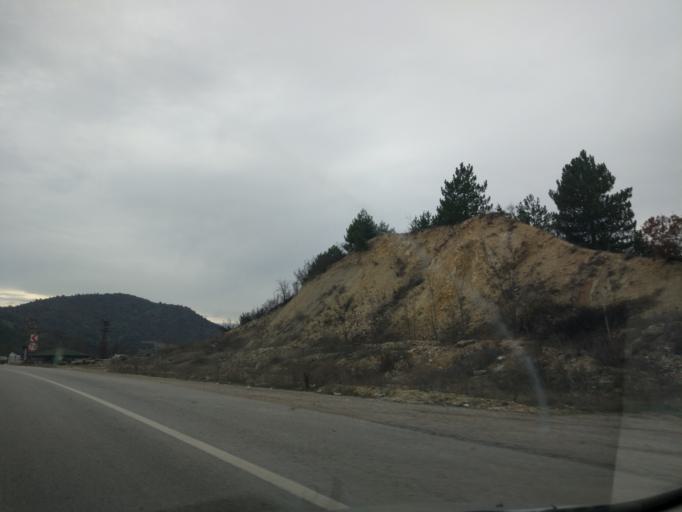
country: TR
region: Karabuk
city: Eskipazar
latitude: 40.9876
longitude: 32.5645
